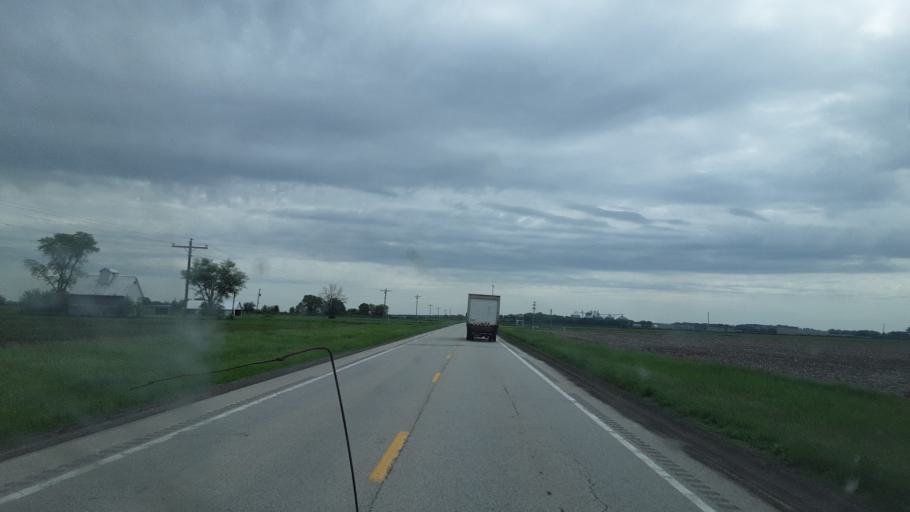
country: US
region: Illinois
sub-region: Mason County
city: Mason City
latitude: 40.3048
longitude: -89.6812
